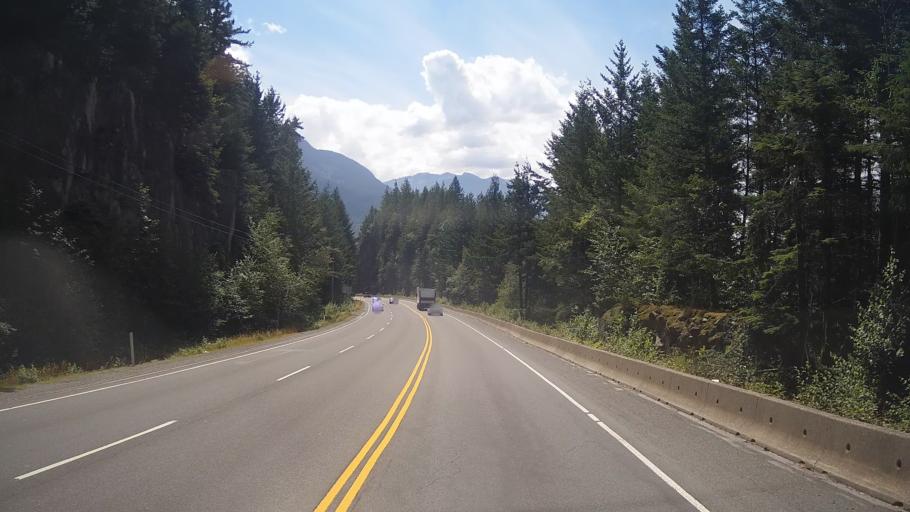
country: CA
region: British Columbia
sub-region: Greater Vancouver Regional District
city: Lions Bay
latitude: 49.6397
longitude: -123.2129
